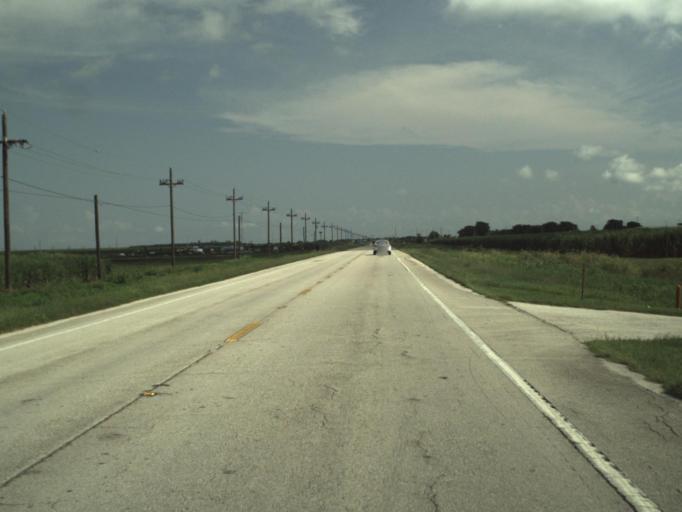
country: US
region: Florida
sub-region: Palm Beach County
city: Belle Glade
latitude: 26.7121
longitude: -80.6840
